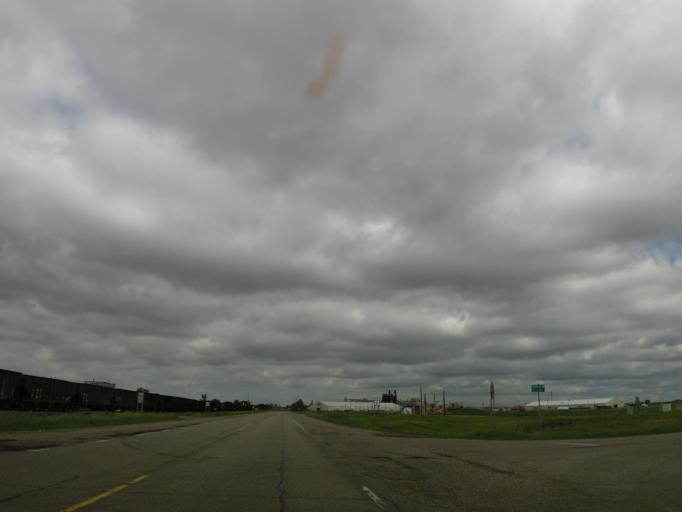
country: US
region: Minnesota
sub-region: Polk County
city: East Grand Forks
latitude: 47.9195
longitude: -96.9928
